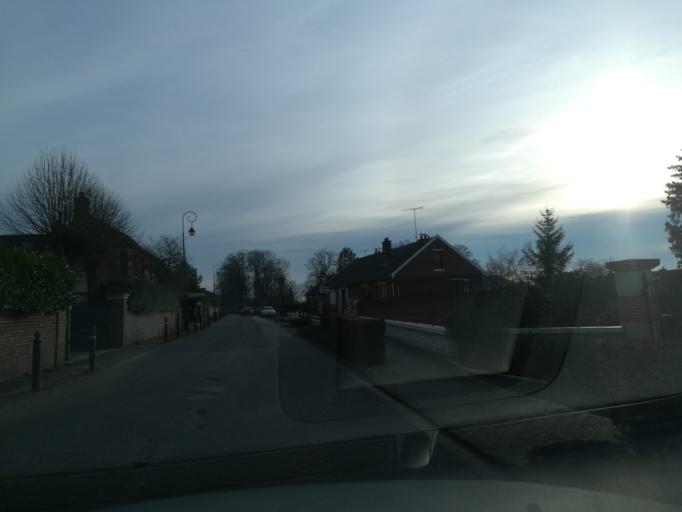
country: FR
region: Haute-Normandie
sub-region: Departement de la Seine-Maritime
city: Saint-Martin-de-Boscherville
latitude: 49.4422
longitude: 0.9637
